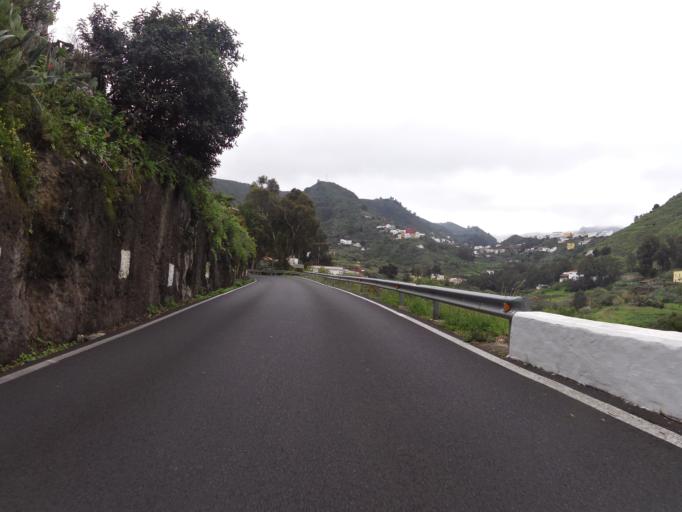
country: ES
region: Canary Islands
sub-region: Provincia de Las Palmas
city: Teror
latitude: 28.0728
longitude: -15.5241
